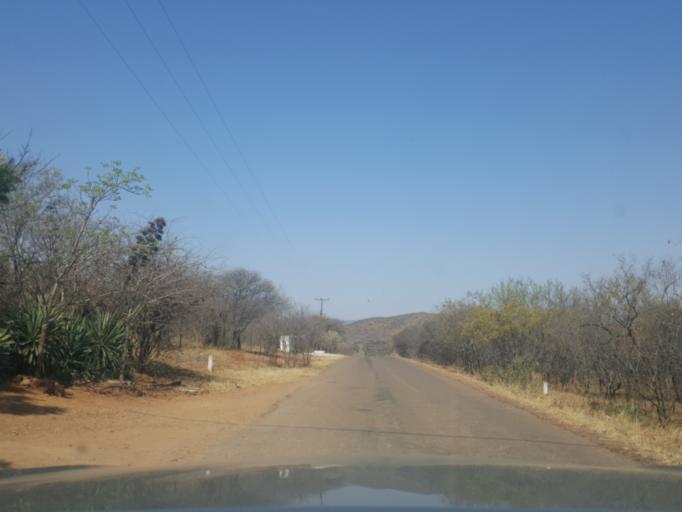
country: BW
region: Kweneng
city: Gabane
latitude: -24.7400
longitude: 25.8182
